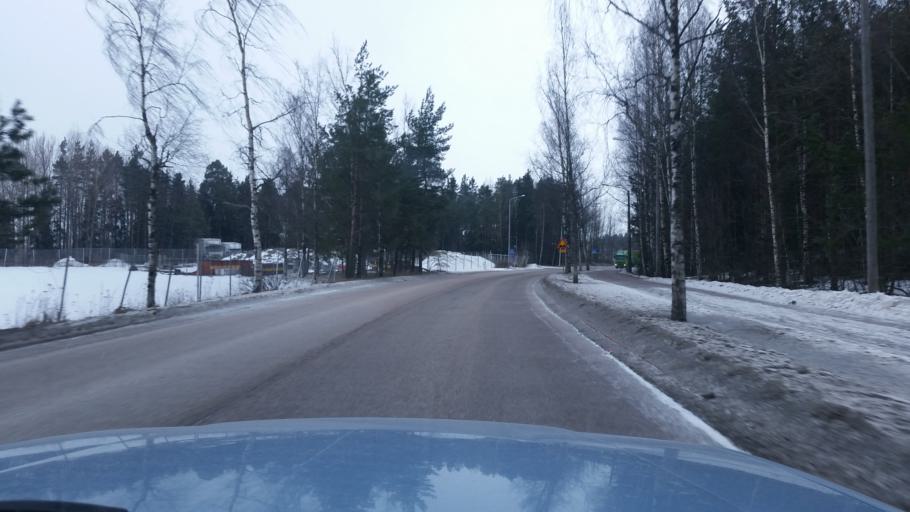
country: FI
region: Uusimaa
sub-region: Helsinki
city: Helsinki
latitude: 60.2185
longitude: 24.9228
